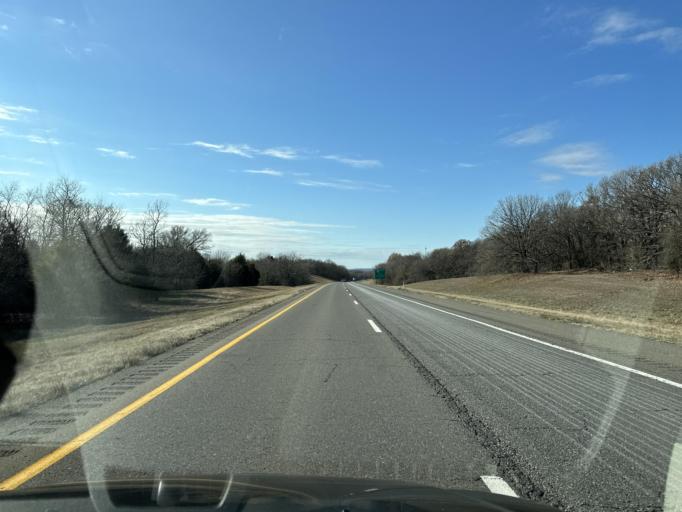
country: US
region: Oklahoma
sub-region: Sequoyah County
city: Vian
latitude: 35.4906
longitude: -95.0678
